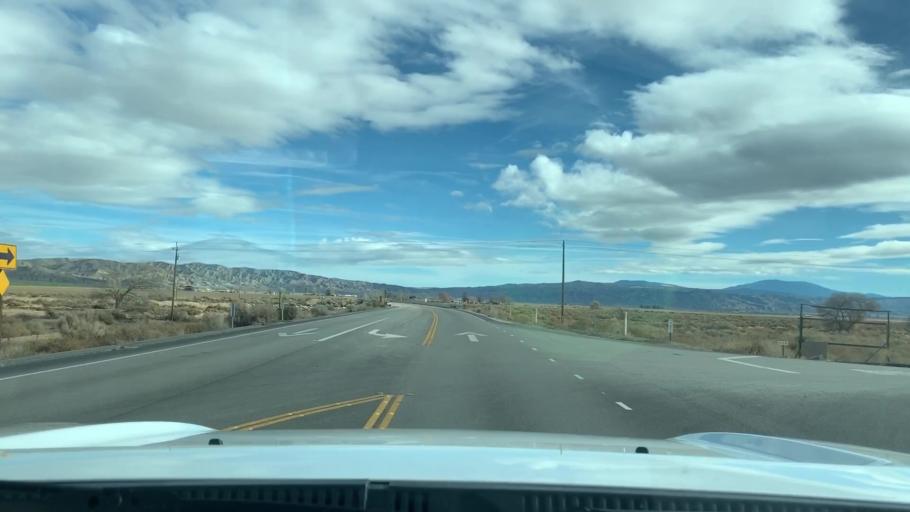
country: US
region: California
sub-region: Kern County
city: Maricopa
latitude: 34.9326
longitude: -119.5964
